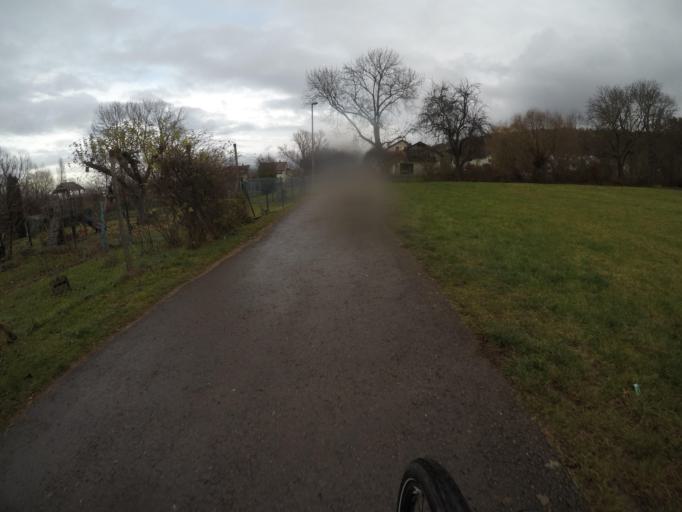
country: DE
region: Baden-Wuerttemberg
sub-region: Regierungsbezirk Stuttgart
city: Gerlingen
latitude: 48.7988
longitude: 9.0793
